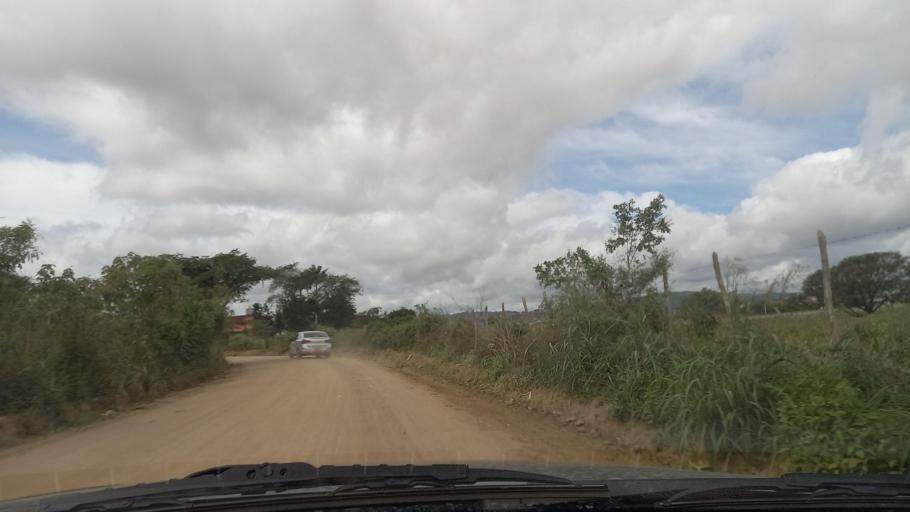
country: BR
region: Pernambuco
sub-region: Gravata
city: Gravata
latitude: -8.1834
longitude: -35.5870
